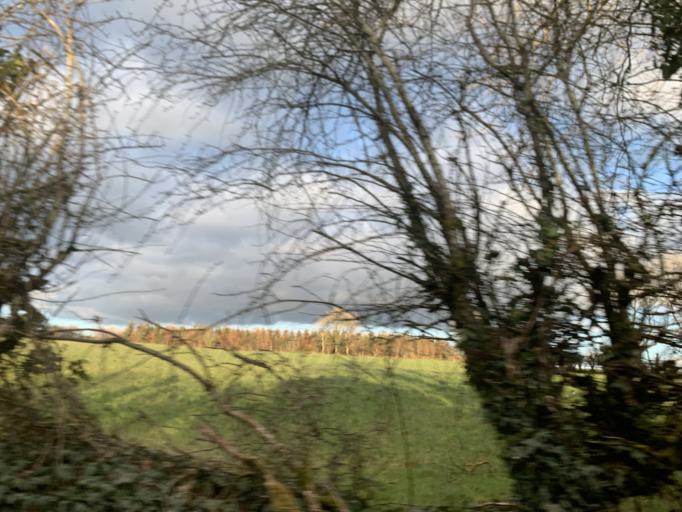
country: IE
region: Connaught
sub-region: Maigh Eo
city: Ballyhaunis
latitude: 53.8171
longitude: -8.6965
